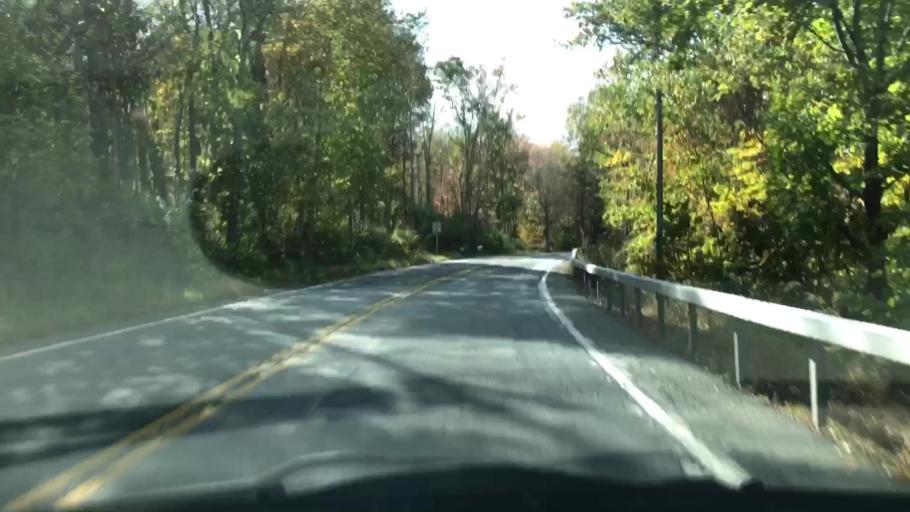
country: US
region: New York
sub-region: Orange County
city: Walden
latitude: 41.5829
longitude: -74.1863
